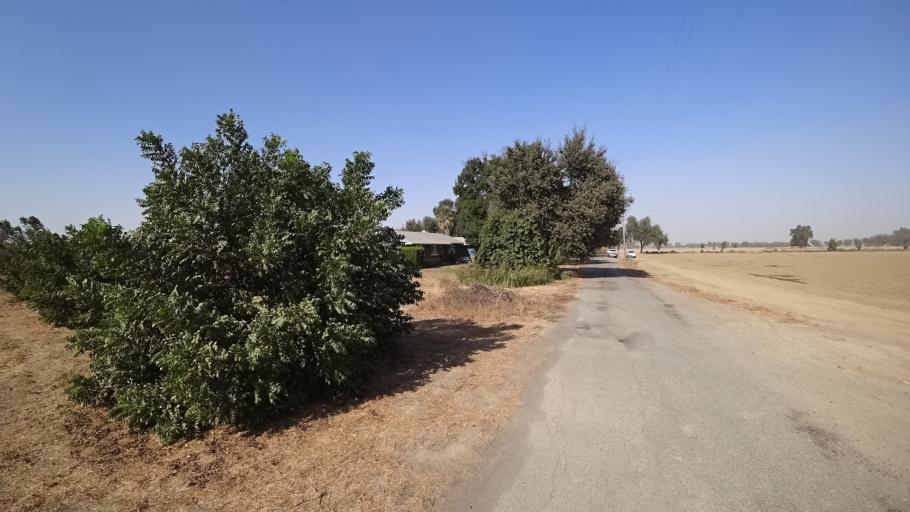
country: US
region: California
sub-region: Yolo County
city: Woodland
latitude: 38.7341
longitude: -121.7813
